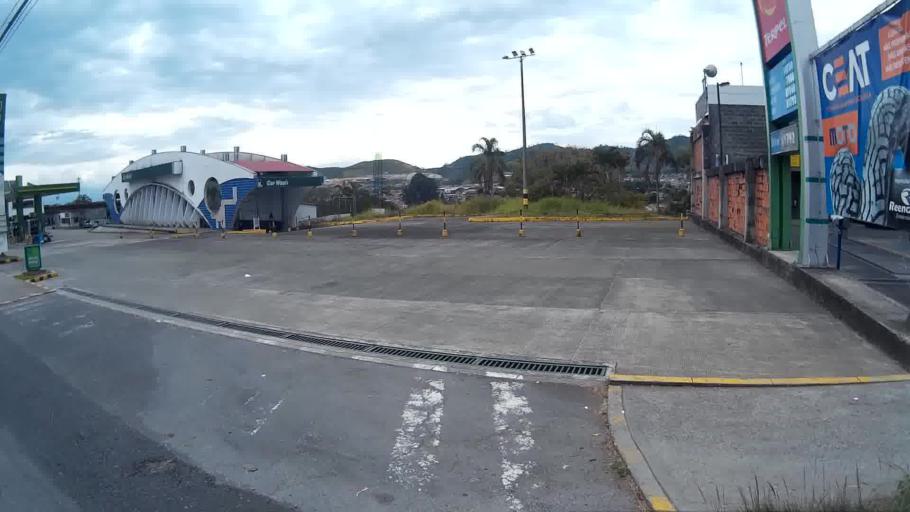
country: CO
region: Risaralda
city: Pereira
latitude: 4.8158
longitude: -75.7259
